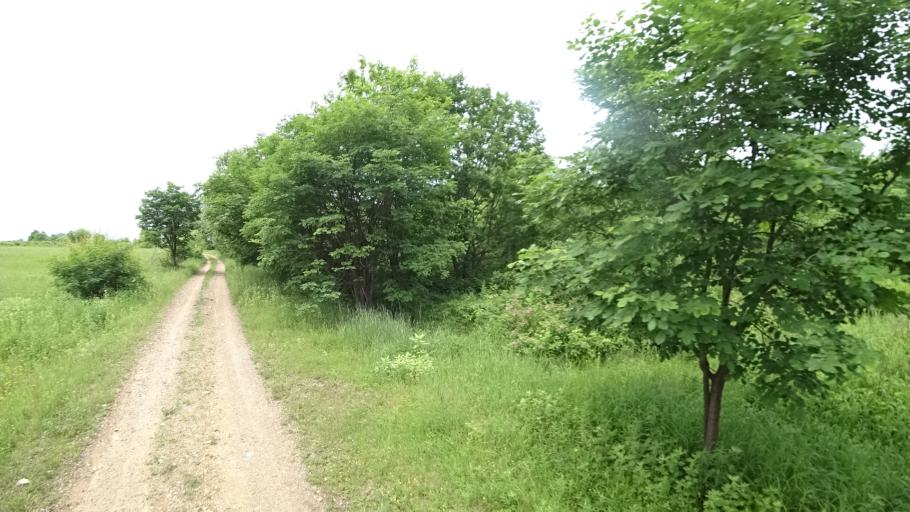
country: RU
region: Primorskiy
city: Arsen'yev
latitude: 44.1829
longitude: 133.3186
